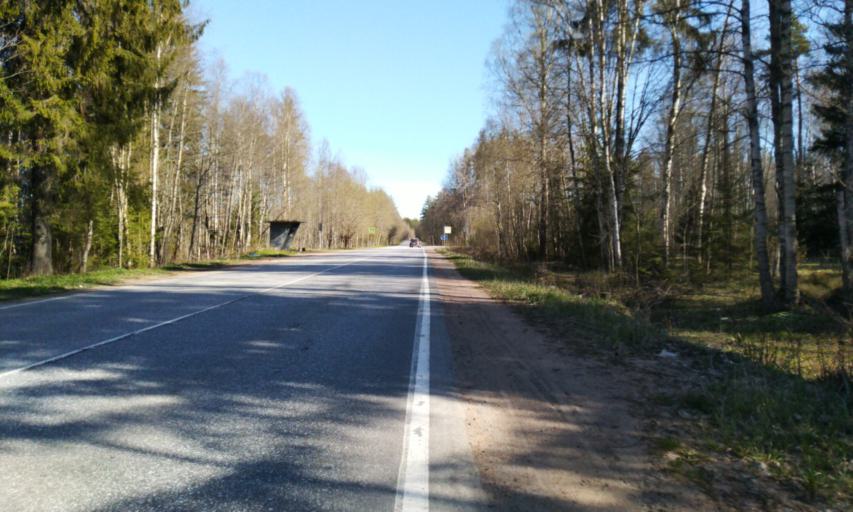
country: RU
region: Leningrad
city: Garbolovo
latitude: 60.3501
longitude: 30.4433
